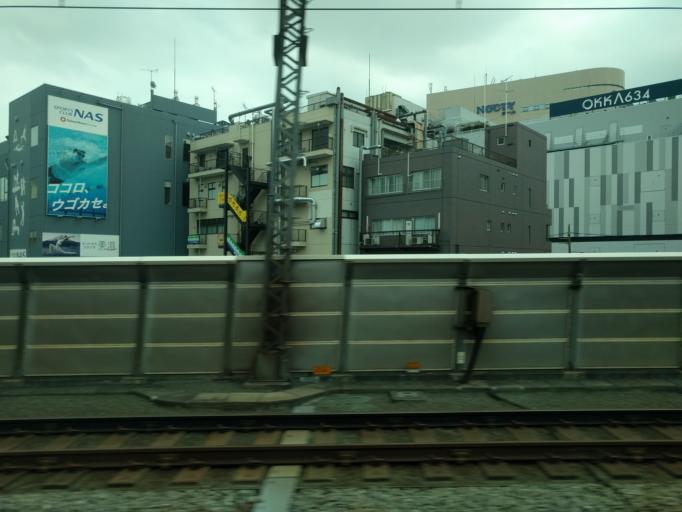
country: JP
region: Tokyo
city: Chofugaoka
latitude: 35.6009
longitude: 139.6124
